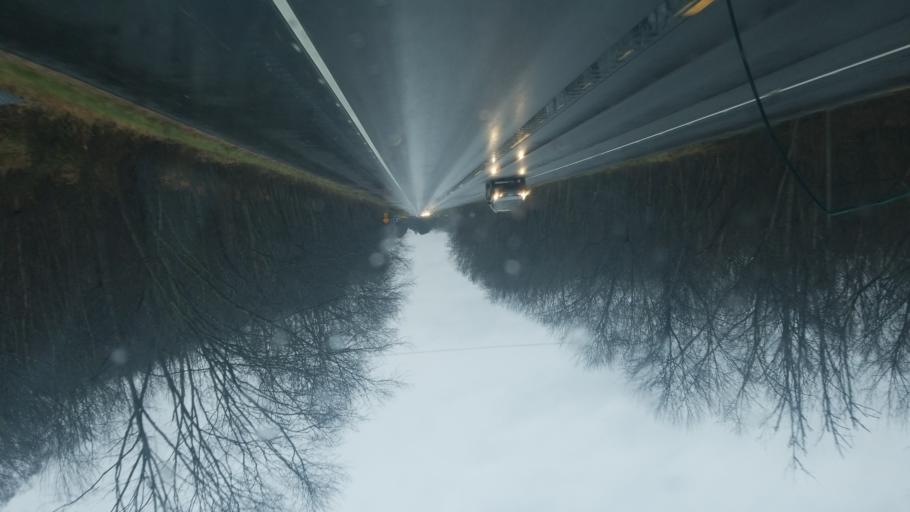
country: US
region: Indiana
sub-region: Brown County
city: Nashville
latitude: 39.1968
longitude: -86.2110
